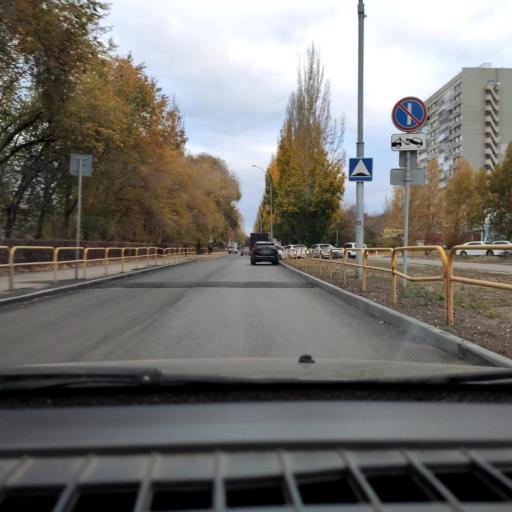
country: RU
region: Samara
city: Tol'yatti
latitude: 53.5211
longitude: 49.3013
